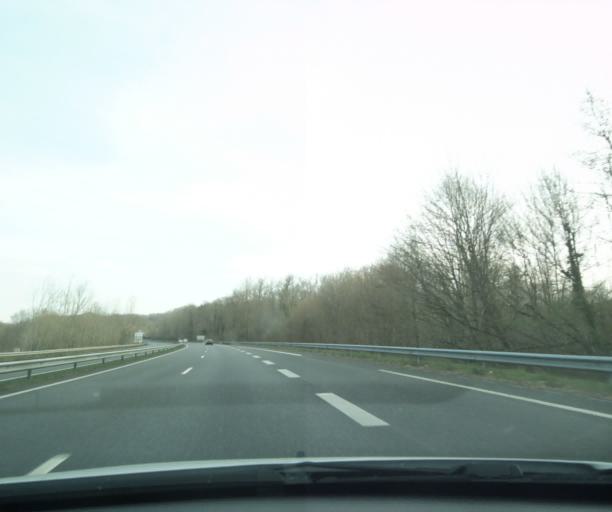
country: FR
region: Midi-Pyrenees
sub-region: Departement des Hautes-Pyrenees
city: Tournay
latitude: 43.1794
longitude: 0.2249
